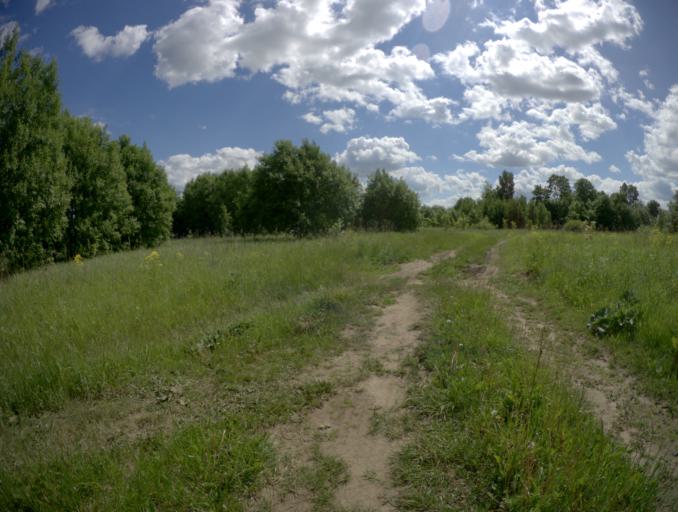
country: RU
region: Ivanovo
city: Gavrilov Posad
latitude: 56.4394
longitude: 40.2481
